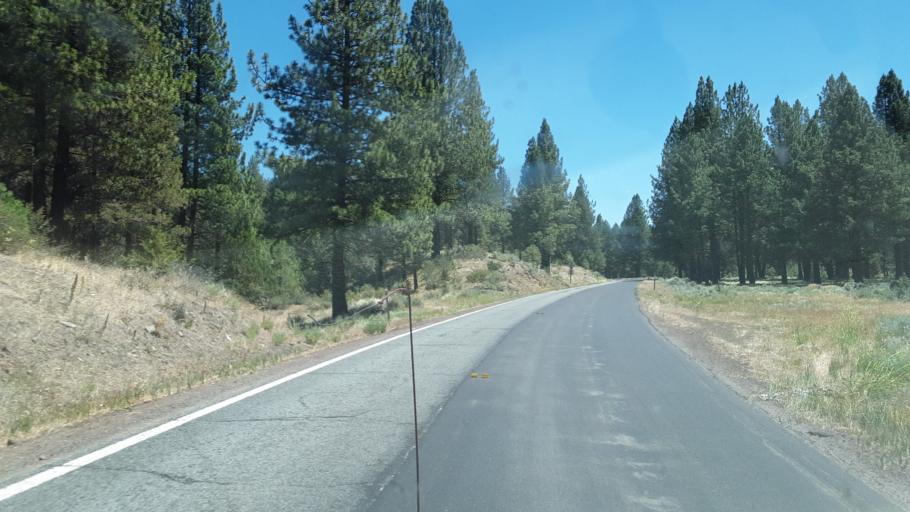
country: US
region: California
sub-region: Modoc County
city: Alturas
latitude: 41.0131
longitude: -120.8224
